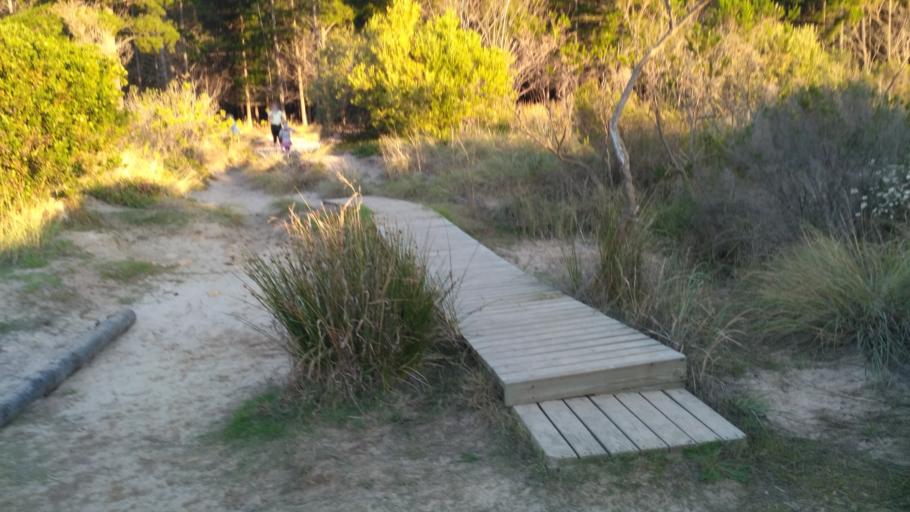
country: ZA
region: Western Cape
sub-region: City of Cape Town
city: Bergvliet
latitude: -34.0548
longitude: 18.4347
